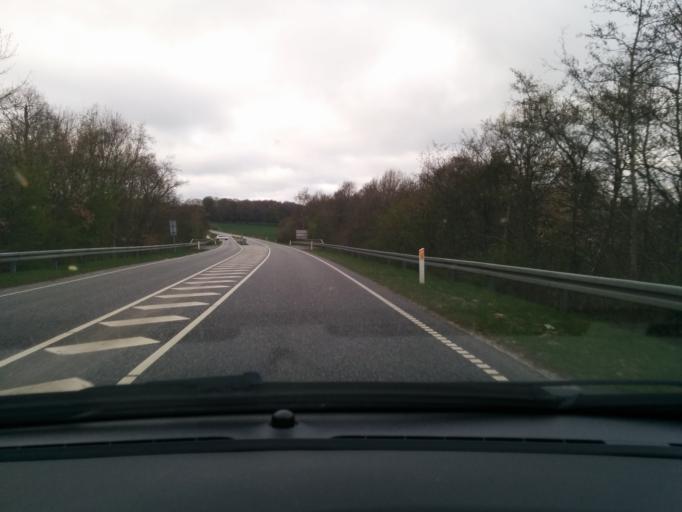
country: DK
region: Central Jutland
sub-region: Favrskov Kommune
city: Hammel
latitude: 56.2594
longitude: 9.8795
